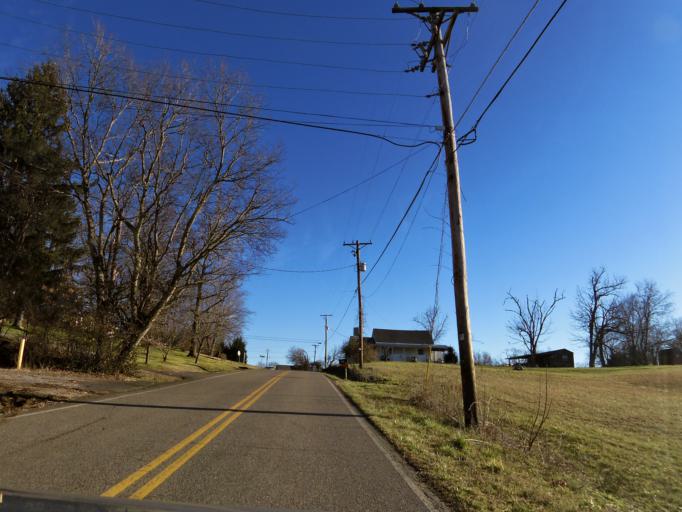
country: US
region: Tennessee
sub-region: Blount County
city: Eagleton Village
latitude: 35.8768
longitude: -83.9385
